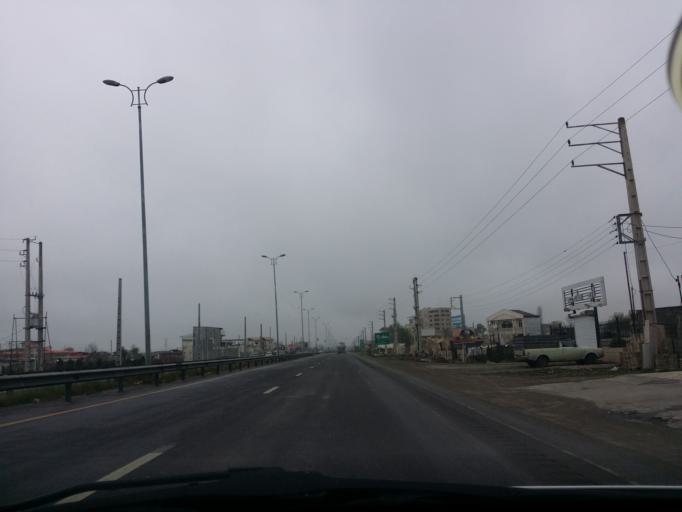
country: IR
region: Mazandaran
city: Tonekabon
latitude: 36.7957
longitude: 50.9146
